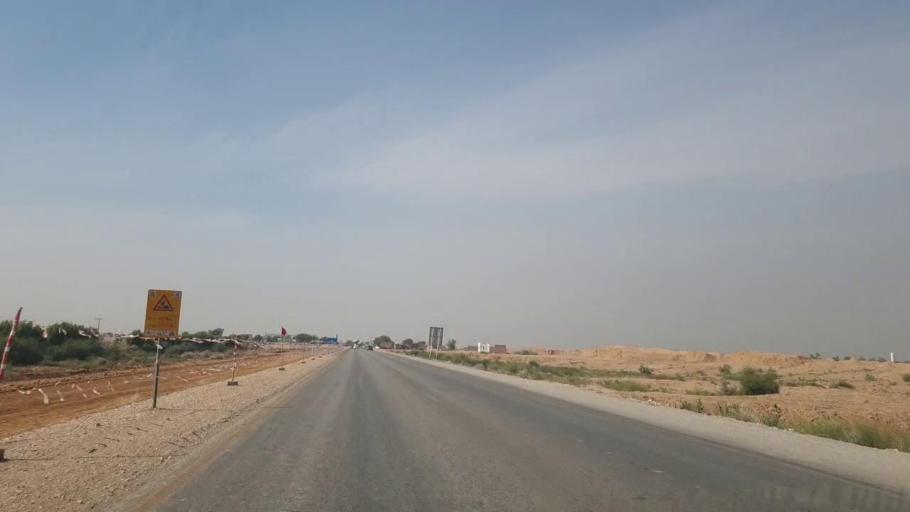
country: PK
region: Sindh
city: Sann
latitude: 26.0250
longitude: 68.1293
